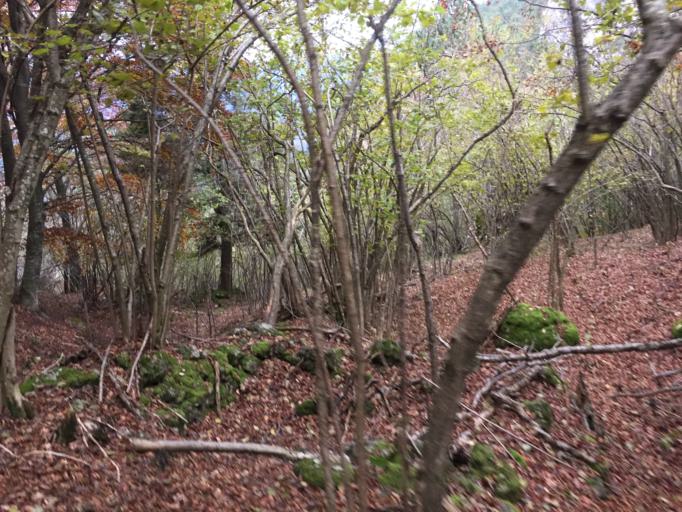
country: IT
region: Friuli Venezia Giulia
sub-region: Provincia di Udine
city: Chiusaforte
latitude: 46.4189
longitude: 13.3066
